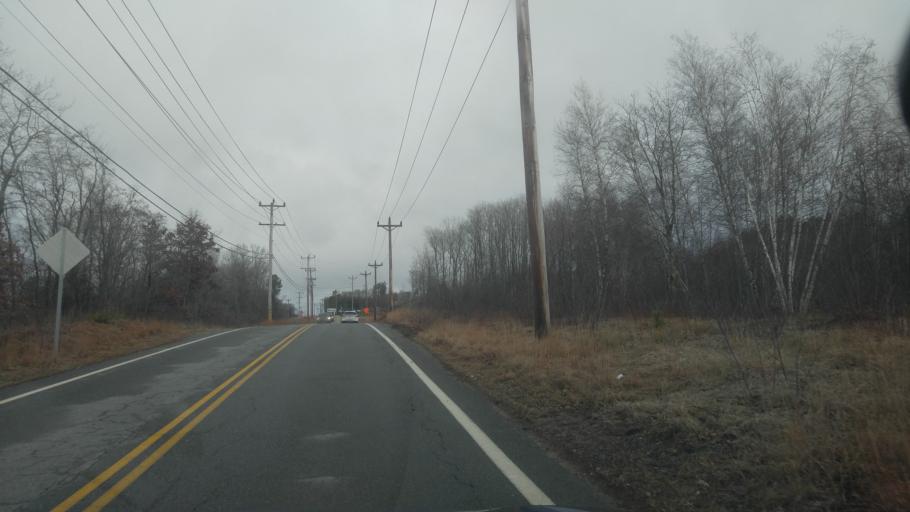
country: US
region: Rhode Island
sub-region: Kent County
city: West Warwick
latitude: 41.6551
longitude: -71.5529
